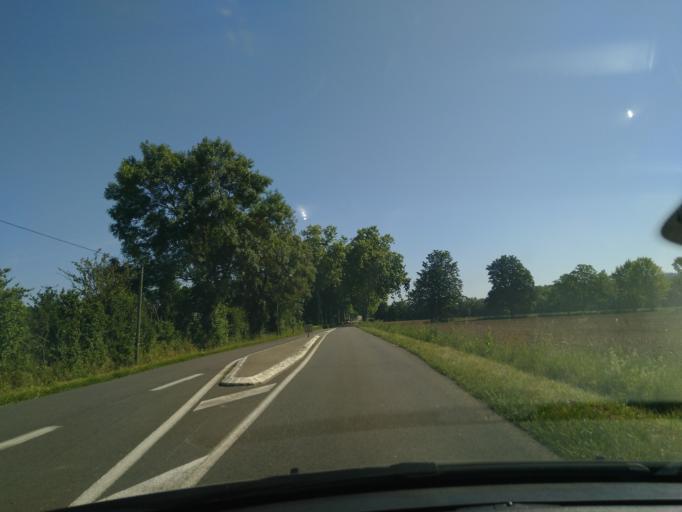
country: FR
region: Midi-Pyrenees
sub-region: Departement du Gers
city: Aubiet
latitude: 43.5762
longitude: 0.8157
